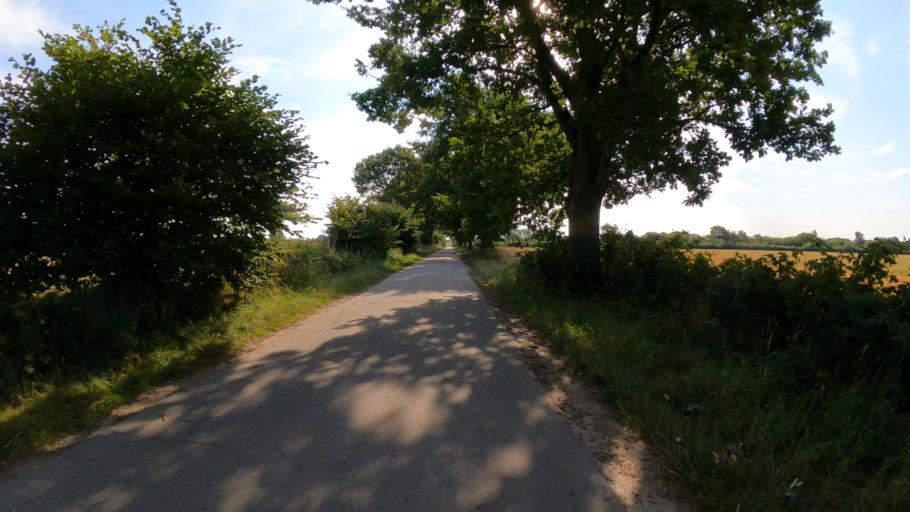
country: DE
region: Schleswig-Holstein
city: Dassendorf
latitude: 53.4958
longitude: 10.3813
